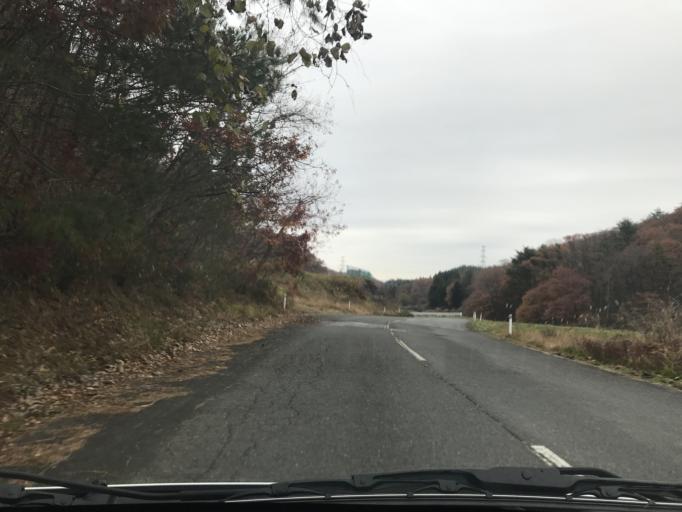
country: JP
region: Iwate
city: Ichinoseki
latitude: 39.0049
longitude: 141.0495
